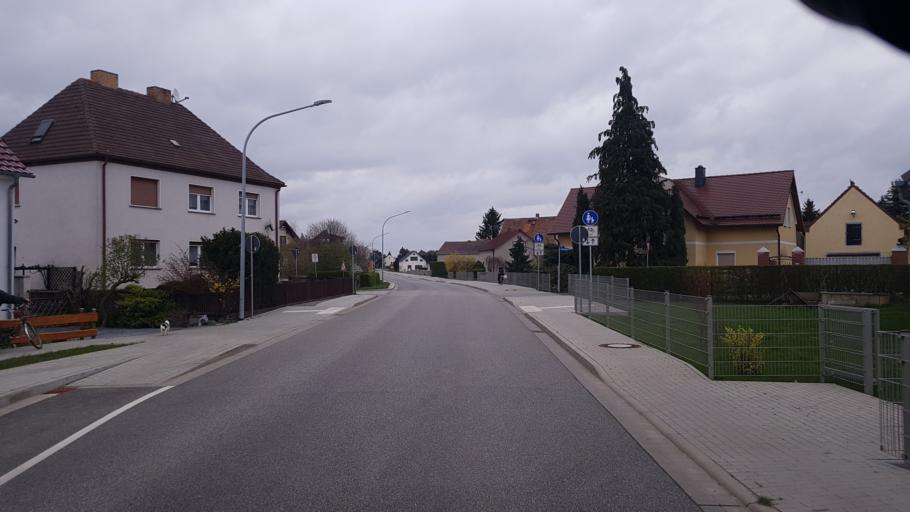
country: DE
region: Brandenburg
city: Hohenbocka
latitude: 51.4548
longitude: 14.0325
